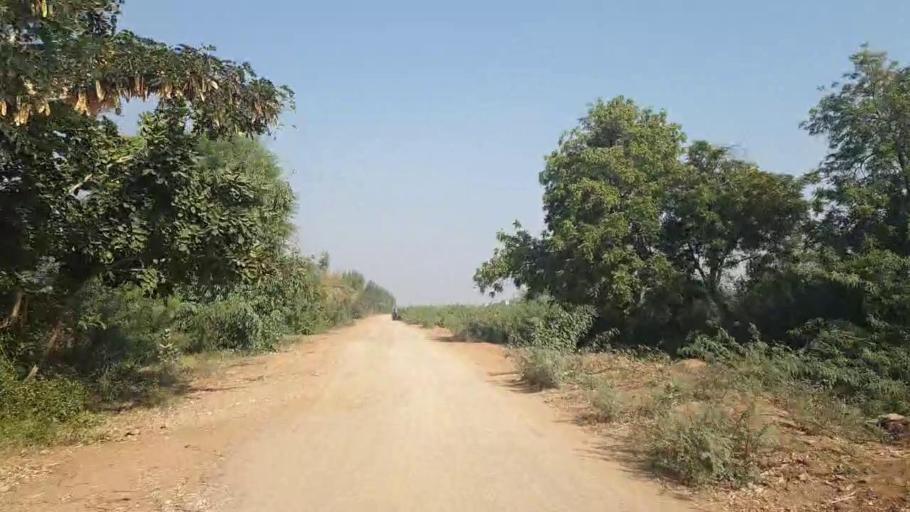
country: PK
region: Sindh
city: Jamshoro
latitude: 25.4591
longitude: 68.2866
